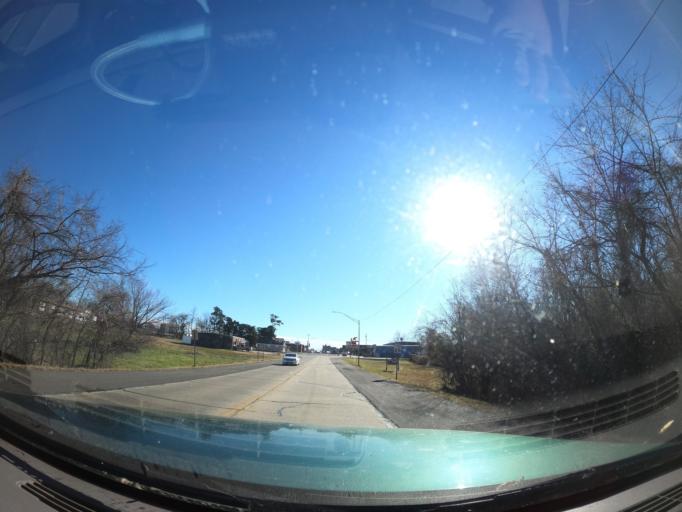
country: US
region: Oklahoma
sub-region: McIntosh County
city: Eufaula
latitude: 35.2914
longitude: -95.5824
